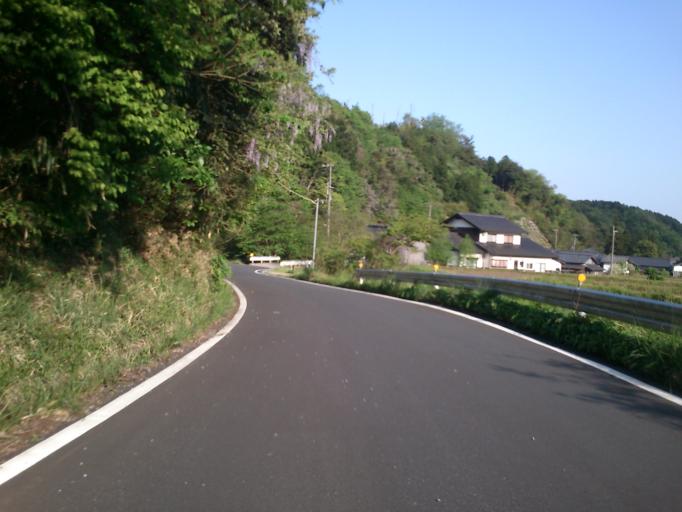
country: JP
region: Kyoto
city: Miyazu
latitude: 35.6140
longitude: 135.1321
